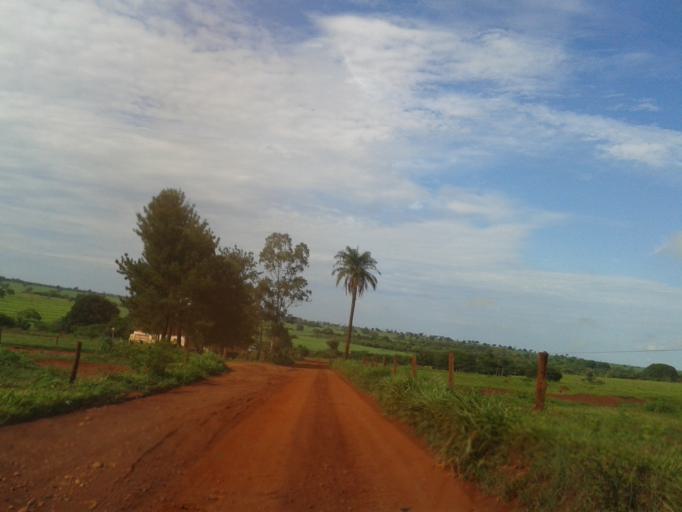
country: BR
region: Minas Gerais
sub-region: Santa Vitoria
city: Santa Vitoria
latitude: -19.2163
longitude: -50.6743
